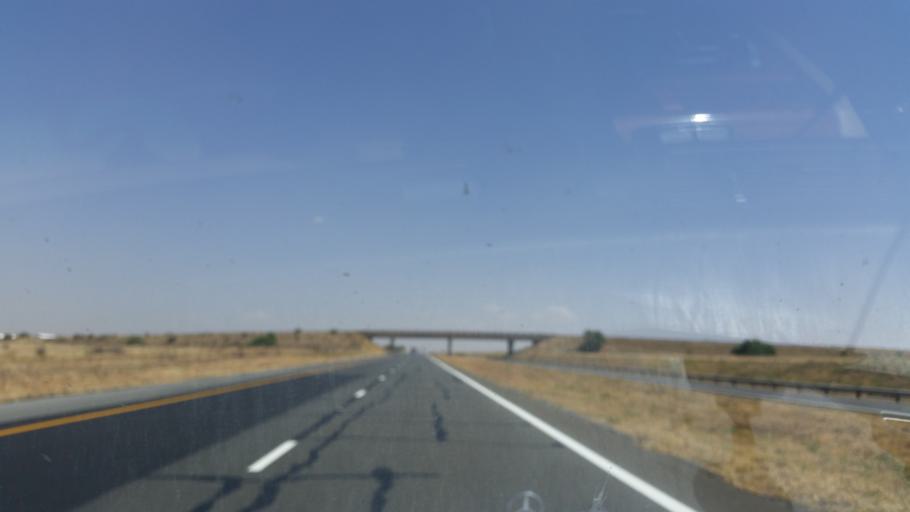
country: ZA
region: Orange Free State
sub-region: Lejweleputswa District Municipality
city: Brandfort
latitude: -28.8657
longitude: 26.5339
